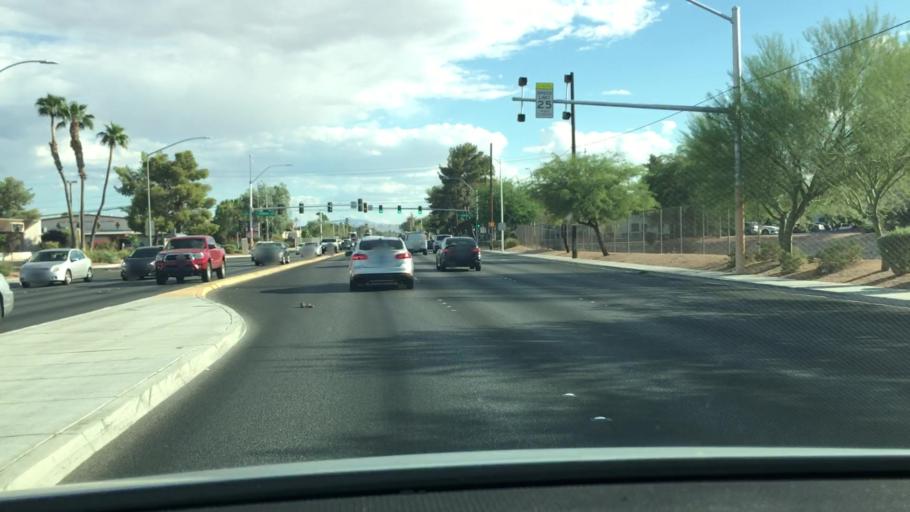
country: US
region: Nevada
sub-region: Clark County
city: Spring Valley
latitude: 36.1530
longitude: -115.2257
